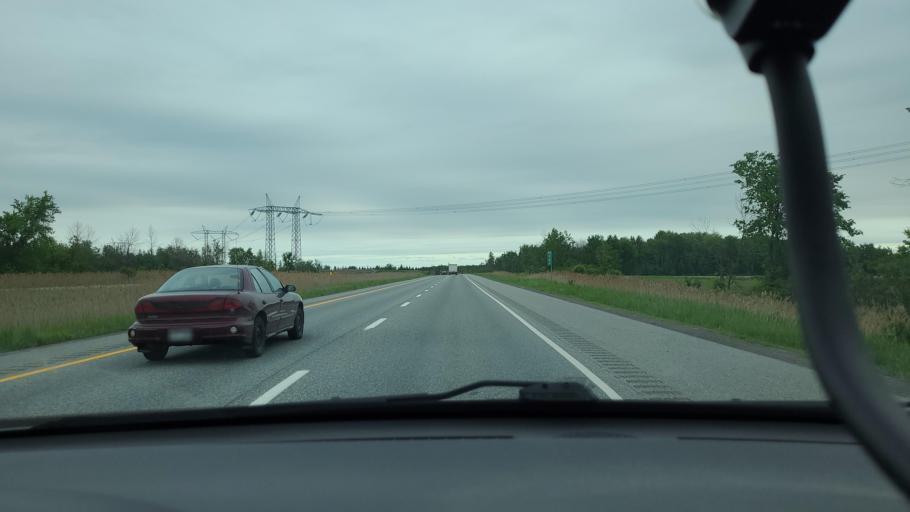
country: CA
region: Quebec
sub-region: Lanaudiere
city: Mascouche
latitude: 45.7742
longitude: -73.5743
